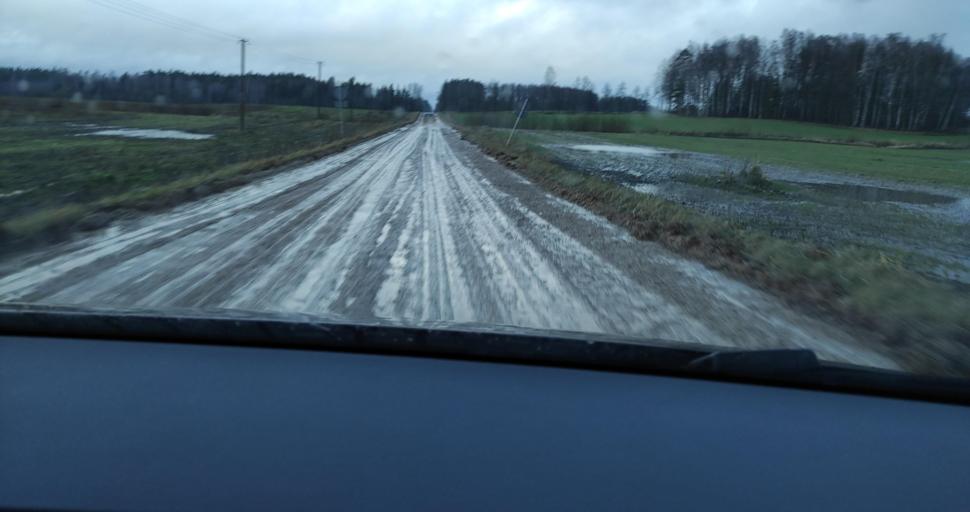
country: LV
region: Skrunda
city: Skrunda
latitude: 56.7146
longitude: 22.2012
